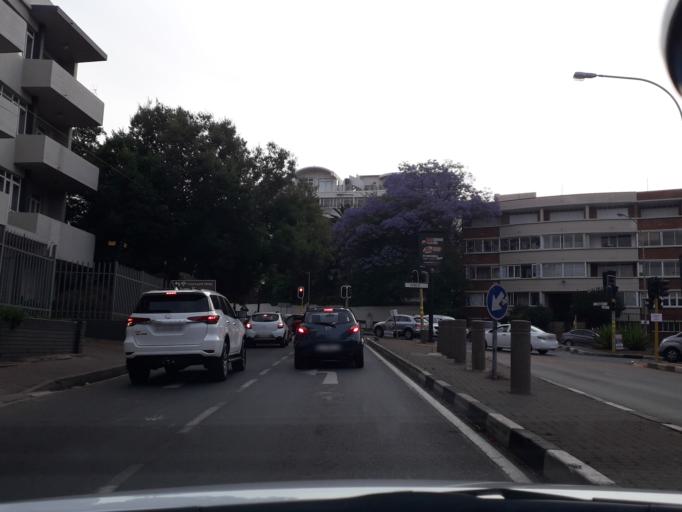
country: ZA
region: Gauteng
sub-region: City of Johannesburg Metropolitan Municipality
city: Johannesburg
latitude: -26.1352
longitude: 28.0485
